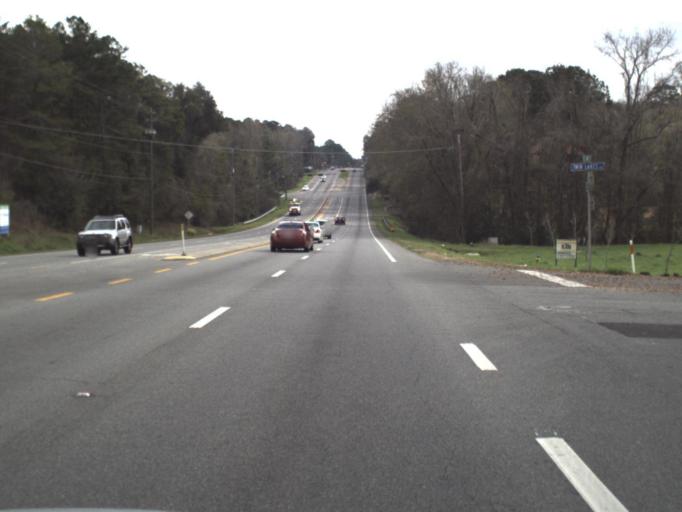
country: US
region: Florida
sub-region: Leon County
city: Tallahassee
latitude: 30.4287
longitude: -84.2057
